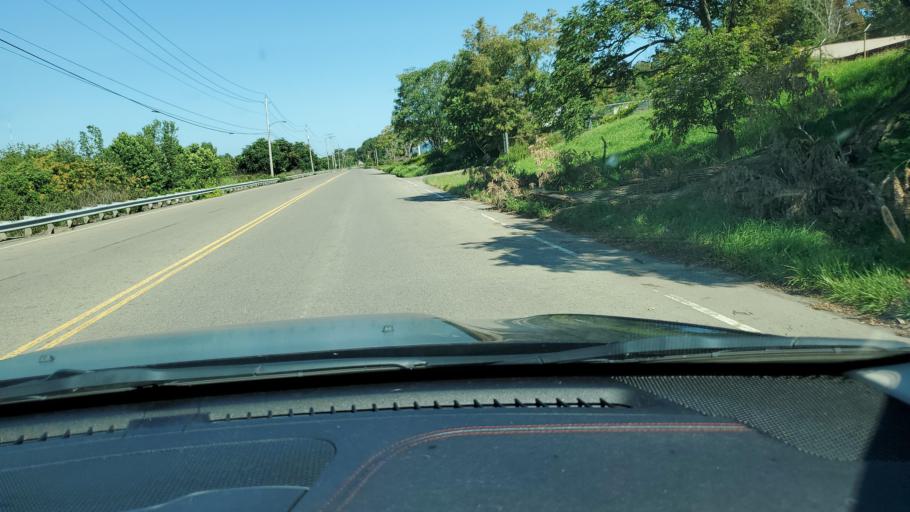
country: US
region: Ohio
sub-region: Mahoning County
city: Campbell
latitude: 41.0670
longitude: -80.5931
